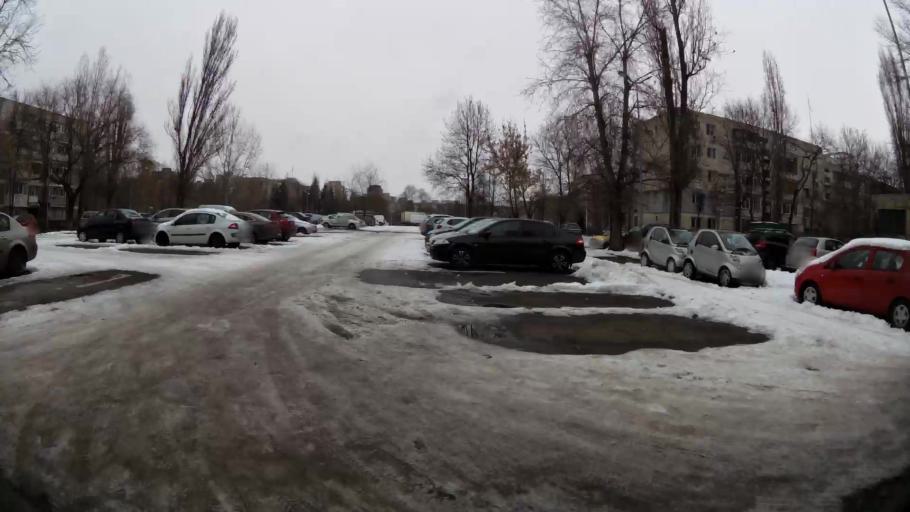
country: RO
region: Ilfov
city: Dobroesti
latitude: 44.4267
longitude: 26.1718
